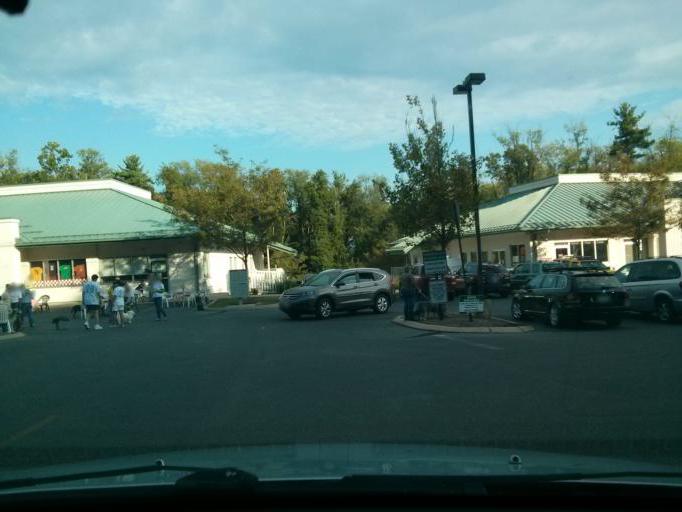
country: US
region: Pennsylvania
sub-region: Centre County
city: Park Forest Village
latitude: 40.8050
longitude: -77.8951
